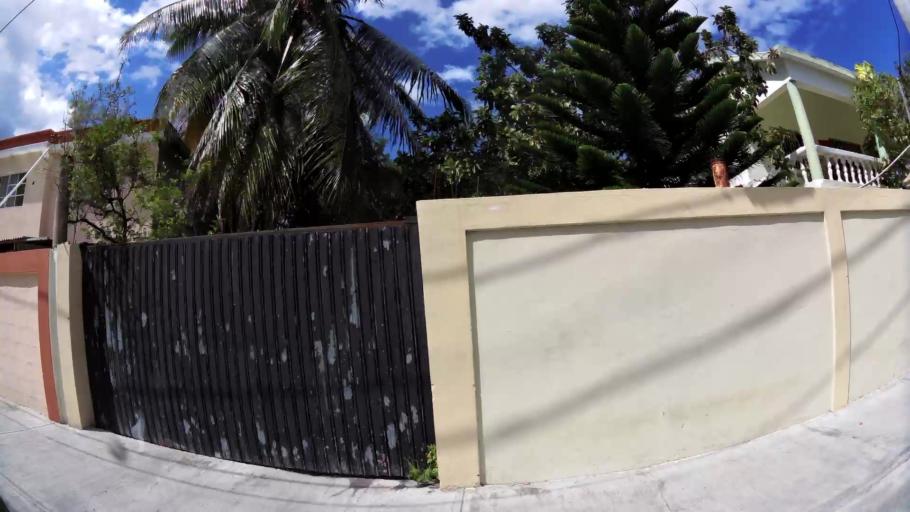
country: DO
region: San Cristobal
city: San Cristobal
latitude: 18.4203
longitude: -70.0923
